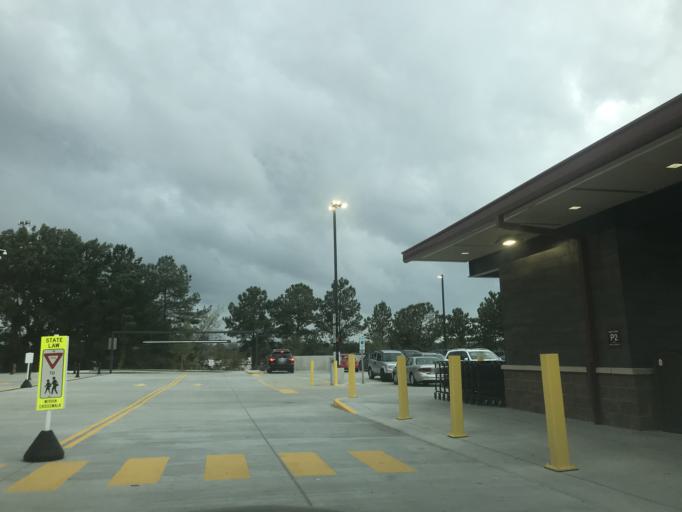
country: US
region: North Carolina
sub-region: Wake County
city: Raleigh
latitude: 35.8210
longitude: -78.6205
